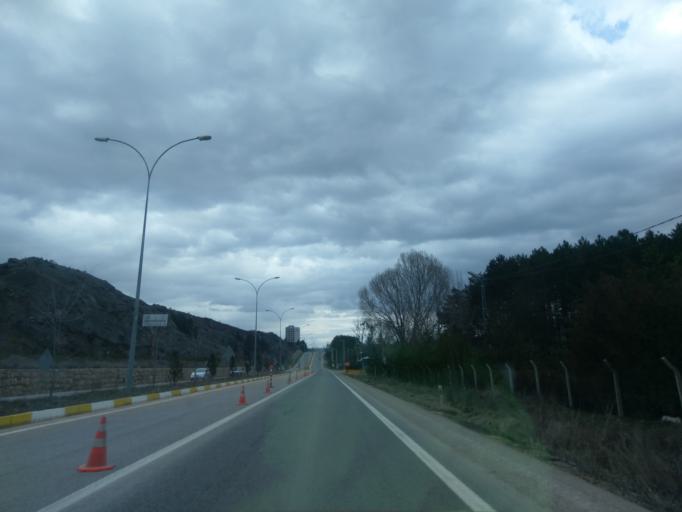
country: TR
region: Eskisehir
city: Eskisehir
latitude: 39.7458
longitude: 30.4341
